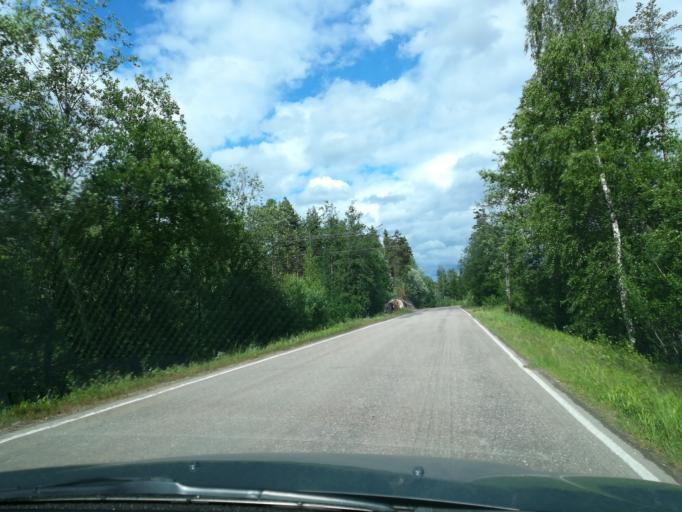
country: FI
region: South Karelia
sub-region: Lappeenranta
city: Savitaipale
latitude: 61.2565
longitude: 27.7140
